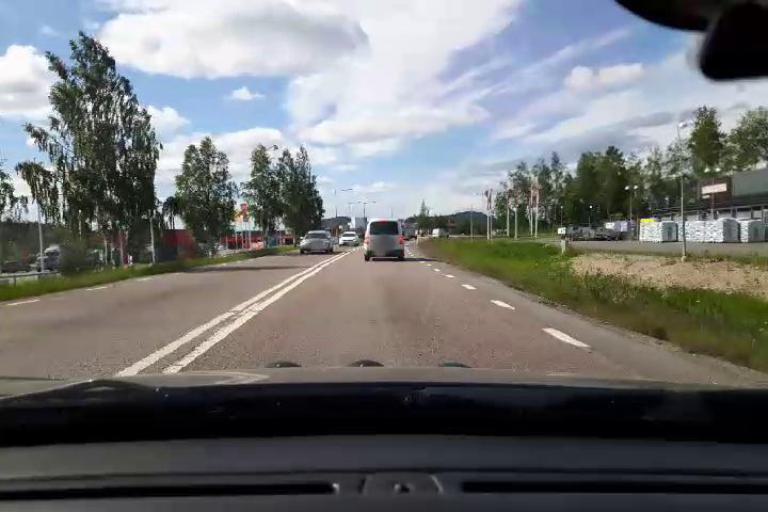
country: SE
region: Gaevleborg
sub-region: Bollnas Kommun
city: Bollnas
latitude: 61.3365
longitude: 16.3986
